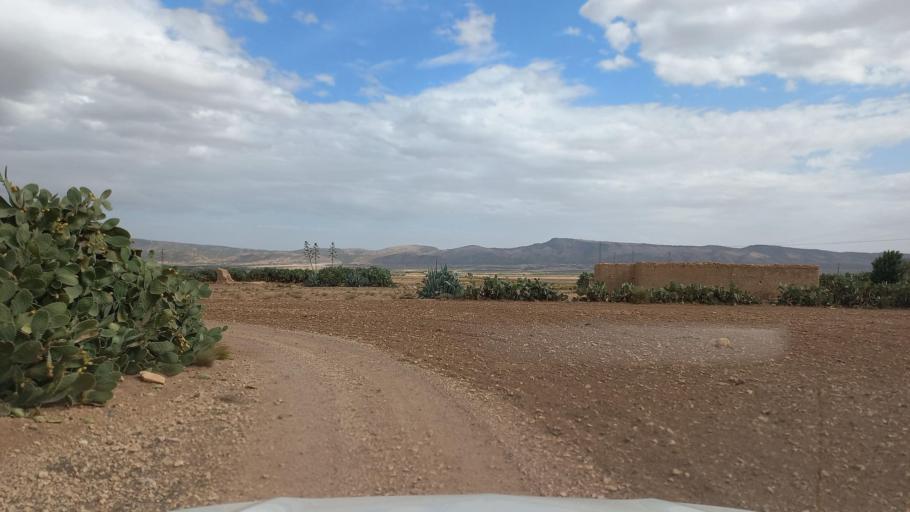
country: TN
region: Al Qasrayn
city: Sbiba
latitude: 35.3868
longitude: 9.1000
